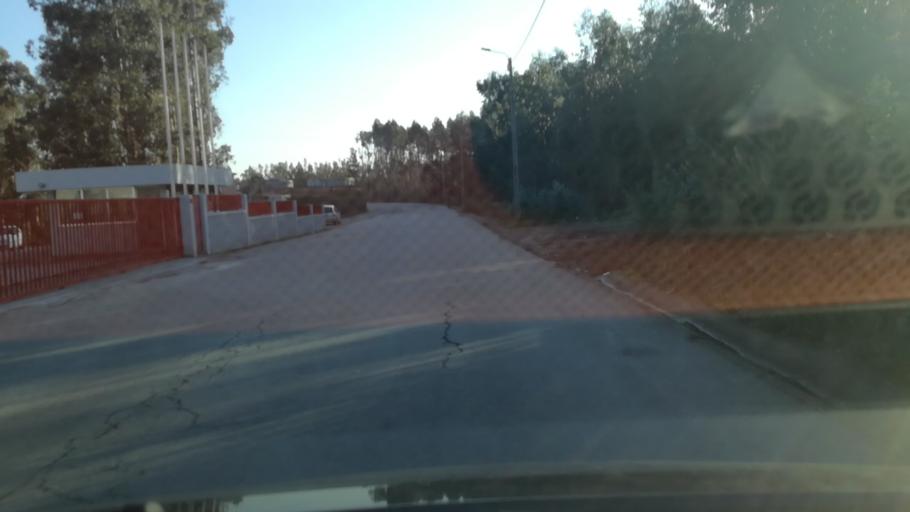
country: PT
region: Braga
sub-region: Vila Nova de Famalicao
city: Ferreiros
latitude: 41.3638
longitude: -8.5329
